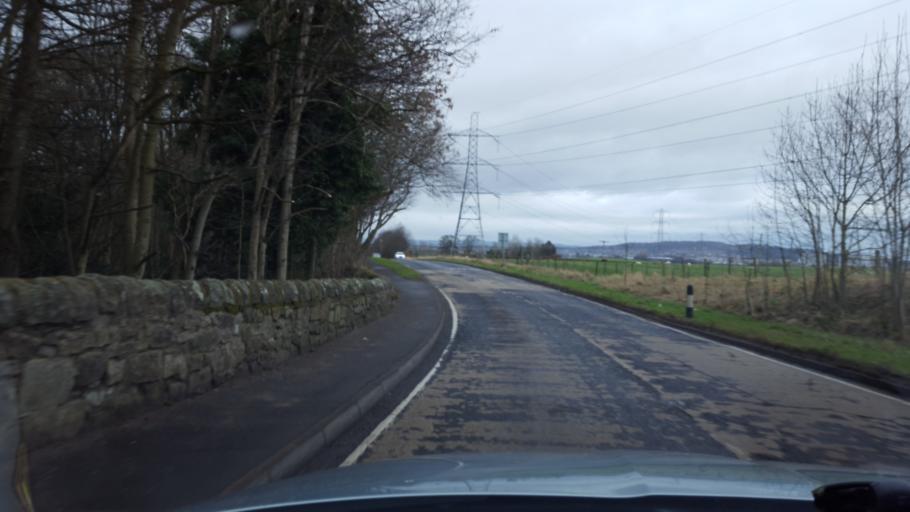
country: GB
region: Scotland
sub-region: Edinburgh
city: Currie
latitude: 55.9072
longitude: -3.3121
